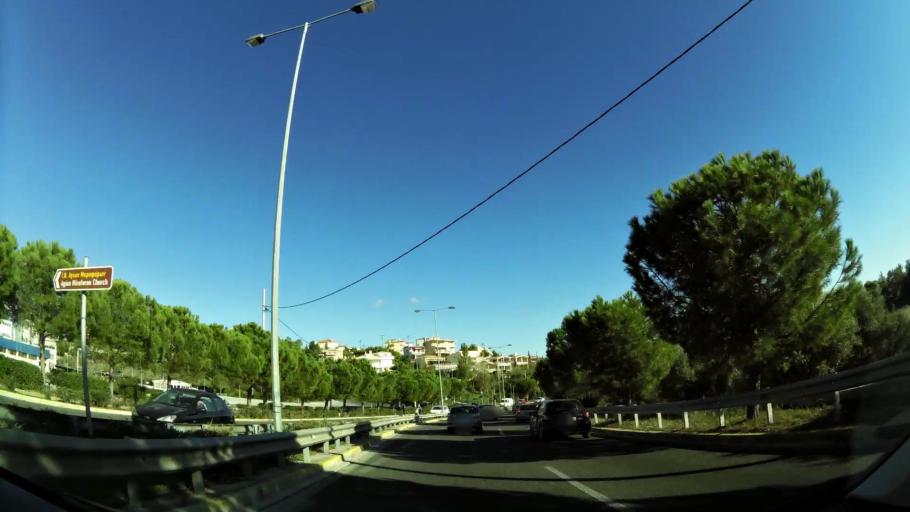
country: GR
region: Attica
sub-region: Nomarchia Anatolikis Attikis
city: Dhrafi
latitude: 38.0024
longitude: 23.9108
